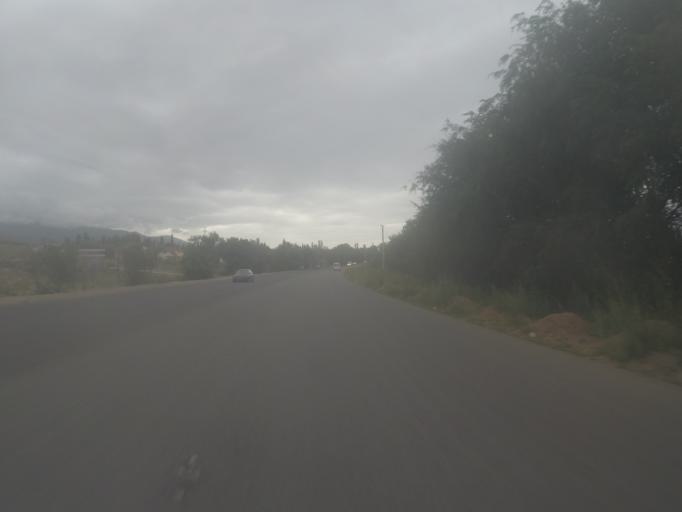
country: KG
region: Ysyk-Koel
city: Cholpon-Ata
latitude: 42.6781
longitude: 77.3123
